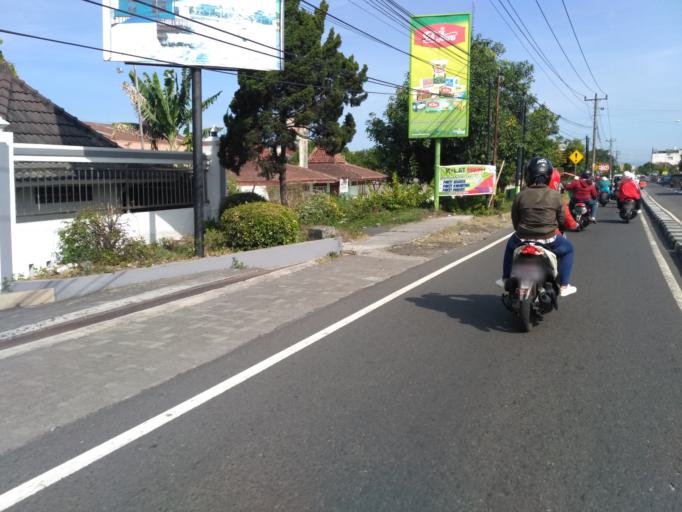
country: ID
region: Daerah Istimewa Yogyakarta
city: Depok
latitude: -7.7681
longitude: 110.4315
